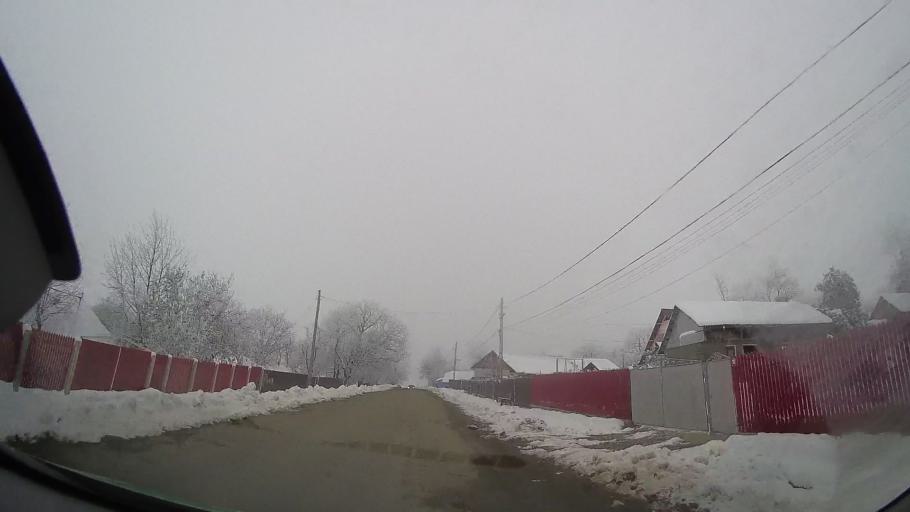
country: RO
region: Iasi
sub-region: Comuna Tansa
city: Suhulet
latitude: 46.8932
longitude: 27.2867
